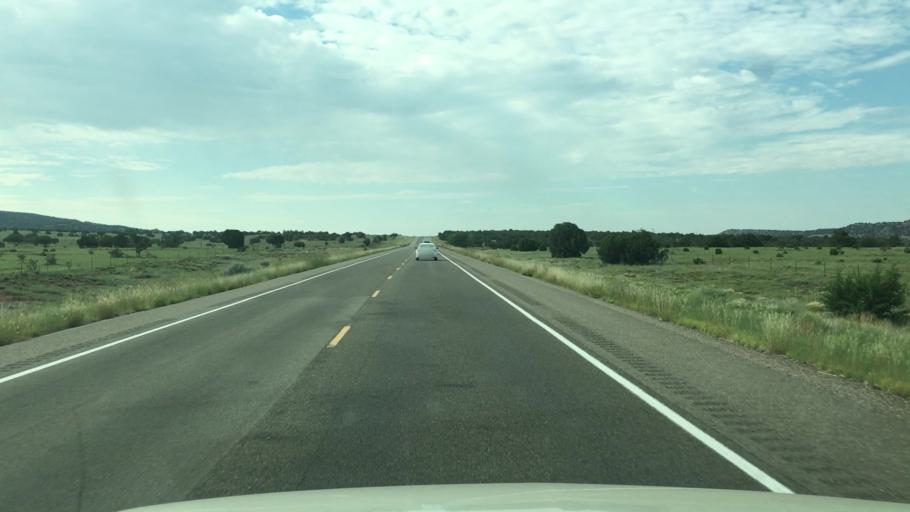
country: US
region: New Mexico
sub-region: Santa Fe County
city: Eldorado at Santa Fe
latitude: 35.3215
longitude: -105.8321
